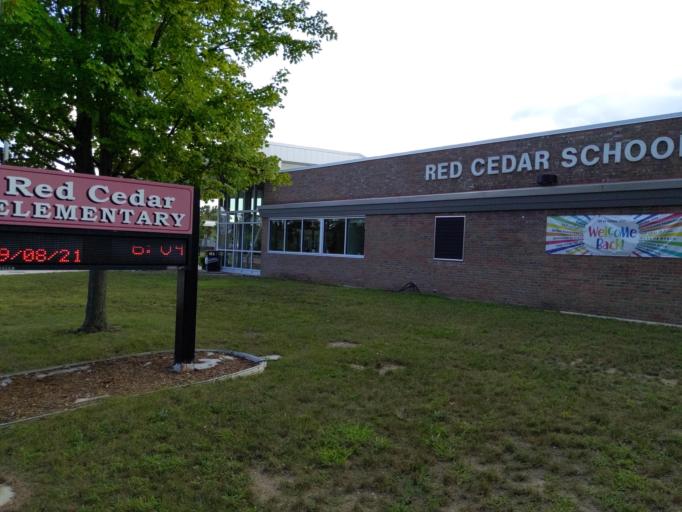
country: US
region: Michigan
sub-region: Ingham County
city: East Lansing
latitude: 42.7221
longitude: -84.4964
